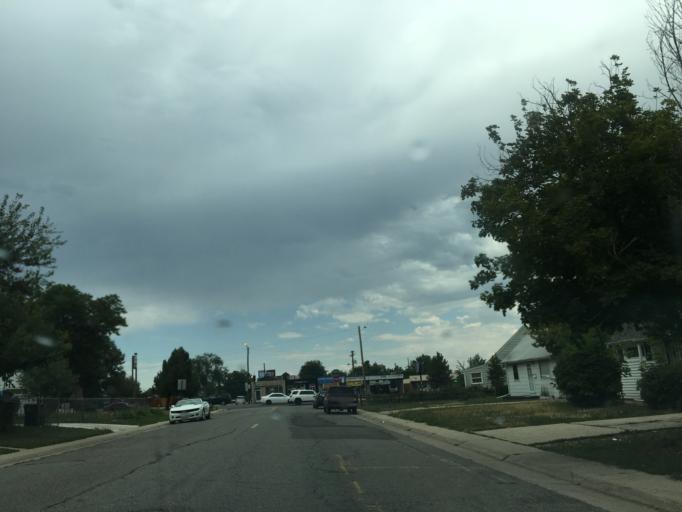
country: US
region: Colorado
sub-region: Arapahoe County
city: Sheridan
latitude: 39.6733
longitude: -105.0262
